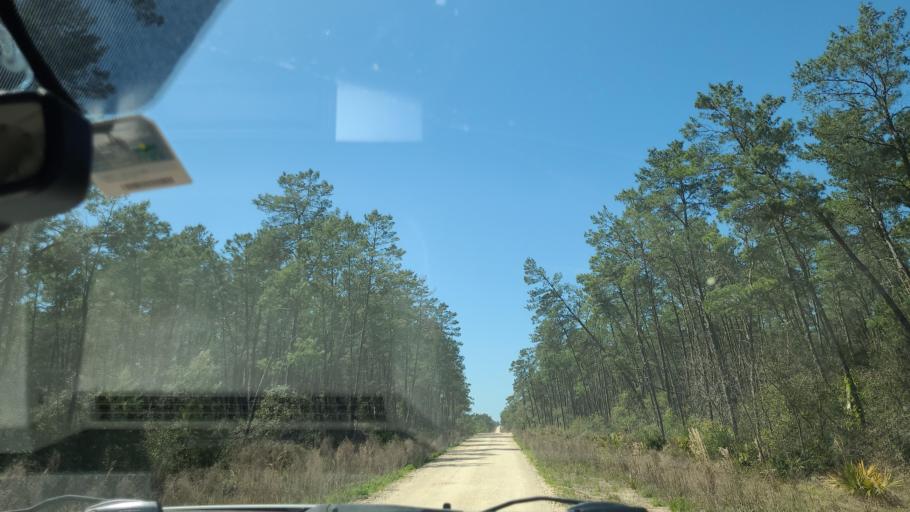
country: US
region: Florida
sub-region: Putnam County
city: Interlachen
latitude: 29.4283
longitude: -81.8871
